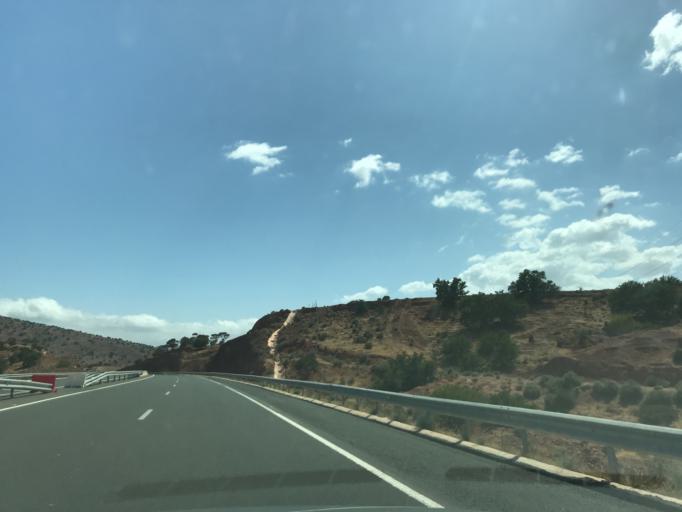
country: MA
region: Souss-Massa-Draa
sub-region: Taroudannt
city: Bigoudine
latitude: 30.7418
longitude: -9.1833
